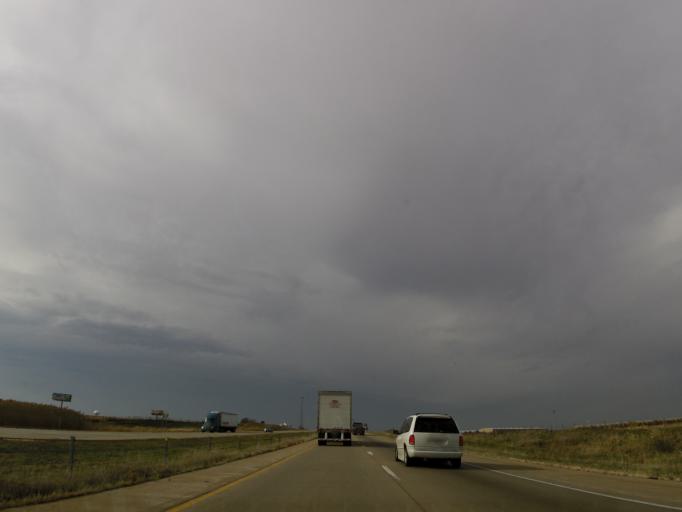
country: US
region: Iowa
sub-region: Scott County
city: Walcott
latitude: 41.6127
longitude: -90.7636
